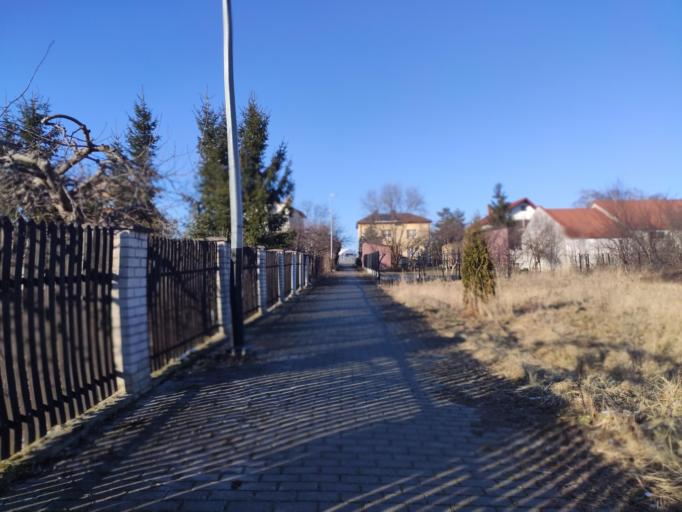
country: PL
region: Lublin Voivodeship
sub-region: Powiat lubartowski
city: Kock
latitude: 51.6425
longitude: 22.4355
